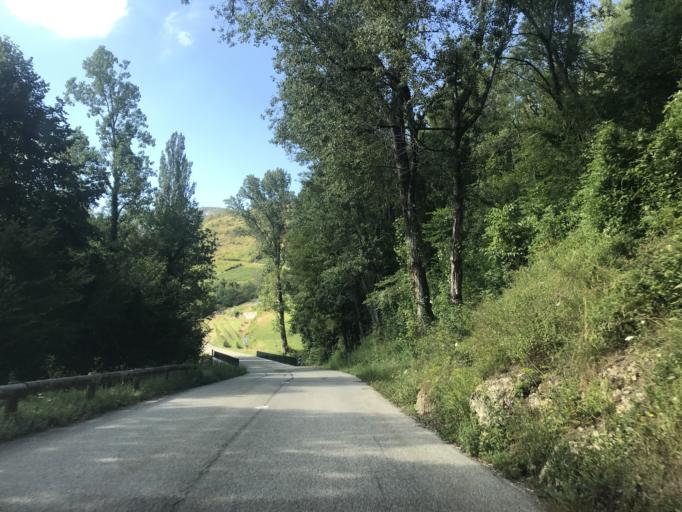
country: FR
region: Rhone-Alpes
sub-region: Departement de la Savoie
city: Le Bourget-du-Lac
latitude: 45.6993
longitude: 5.8351
